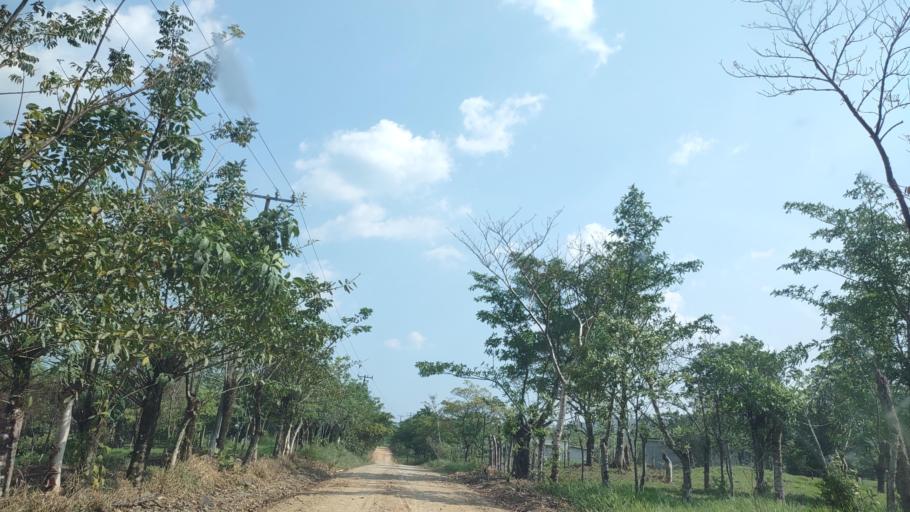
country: MX
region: Chiapas
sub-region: Tecpatan
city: Raudales Malpaso
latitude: 17.3455
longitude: -93.7555
